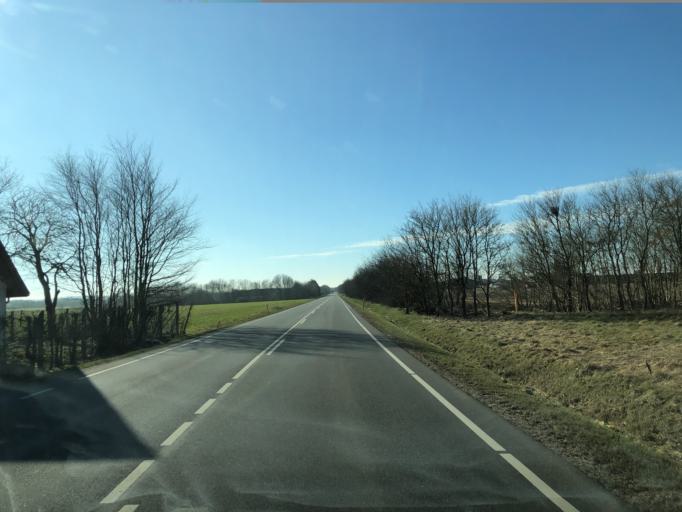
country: DK
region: Central Jutland
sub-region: Ikast-Brande Kommune
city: Bording Kirkeby
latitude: 56.1518
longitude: 9.2301
